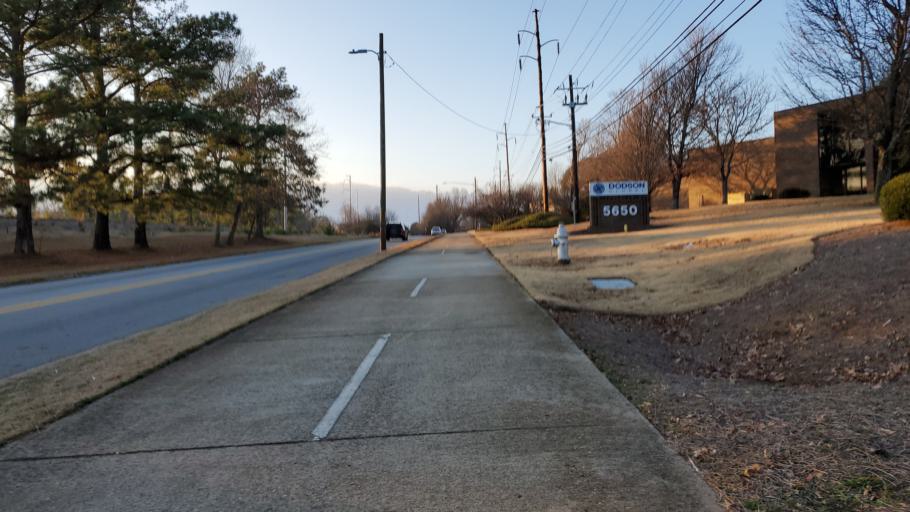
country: US
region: Georgia
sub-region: DeKalb County
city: Stone Mountain
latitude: 33.8232
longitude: -84.1889
